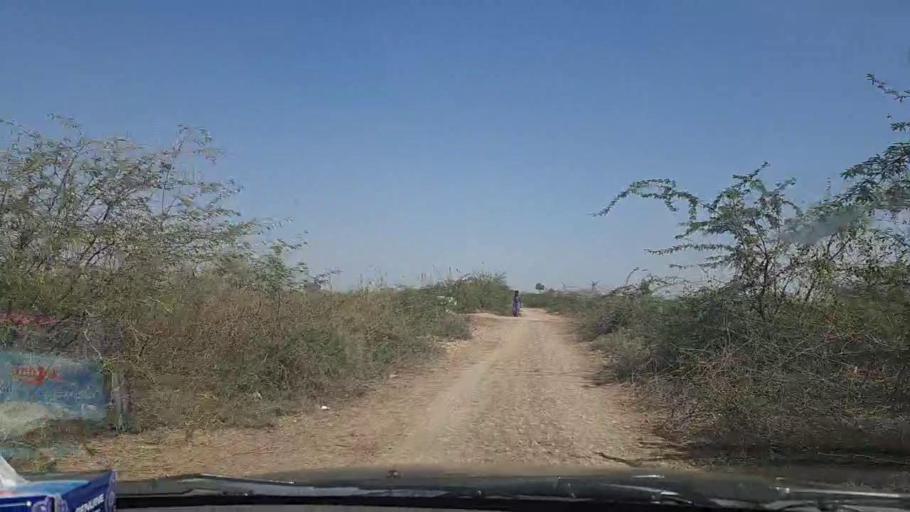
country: PK
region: Sindh
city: Chuhar Jamali
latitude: 24.2741
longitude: 67.7375
